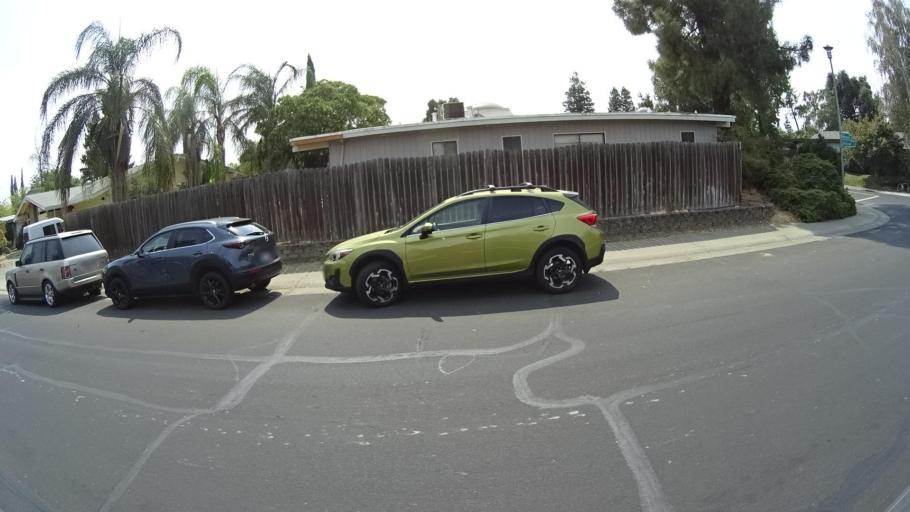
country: US
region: California
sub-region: Sacramento County
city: Elk Grove
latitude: 38.4123
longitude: -121.3784
